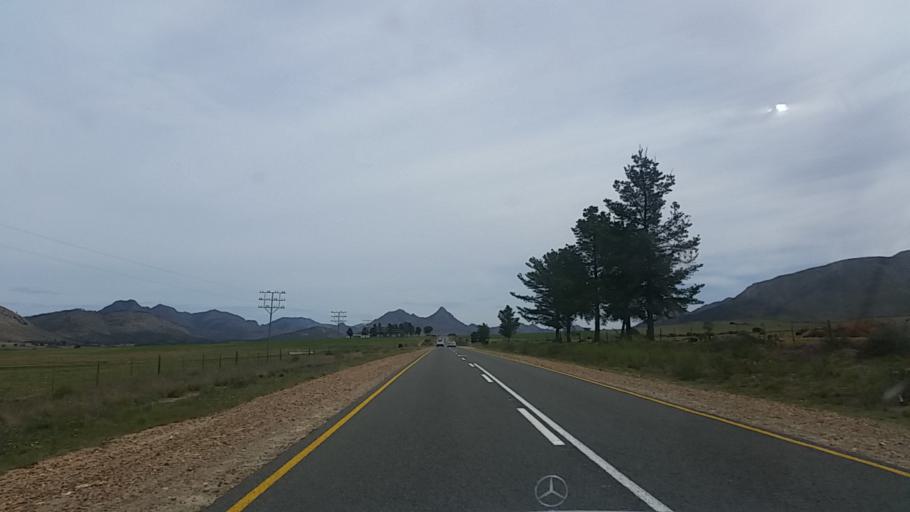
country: ZA
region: Western Cape
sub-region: Eden District Municipality
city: George
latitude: -33.8177
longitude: 22.5073
